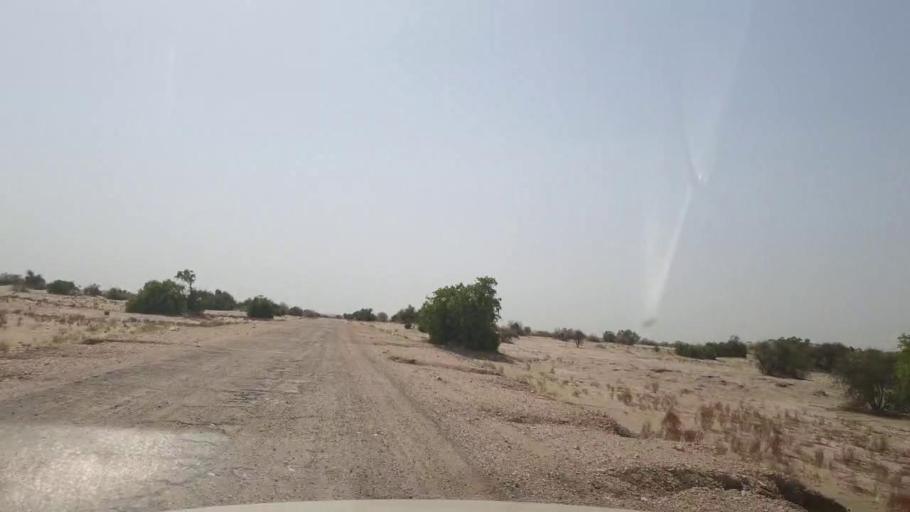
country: PK
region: Sindh
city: Rohri
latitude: 27.4335
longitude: 69.2501
